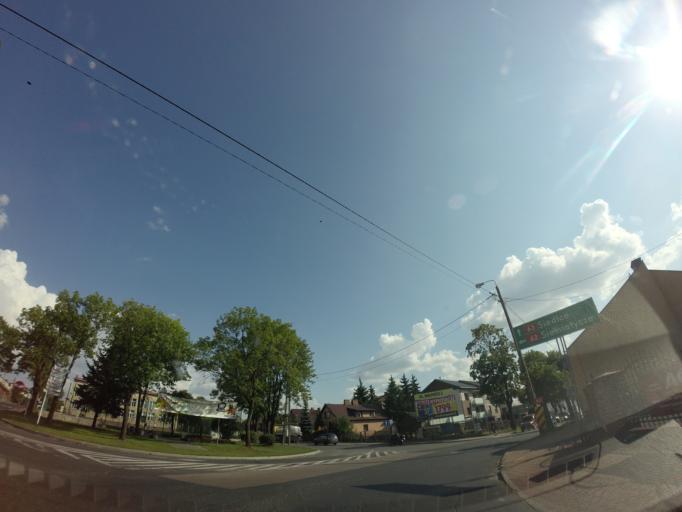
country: PL
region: Masovian Voivodeship
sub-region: Powiat sokolowski
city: Sokolow Podlaski
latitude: 52.4039
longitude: 22.2566
